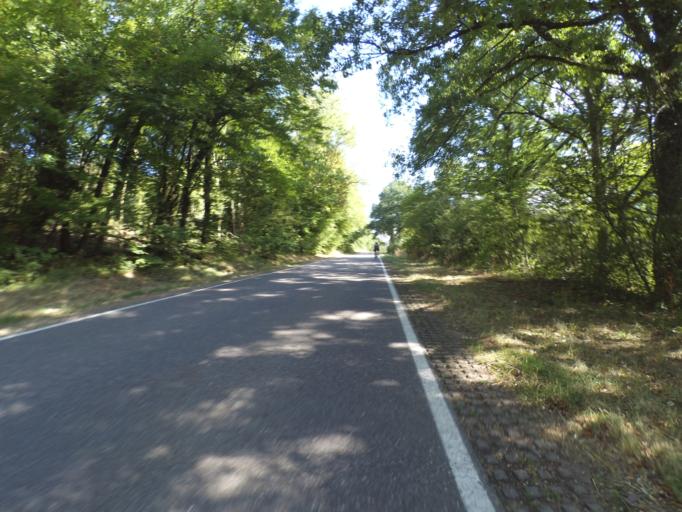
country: DE
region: Saarland
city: Perl
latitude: 49.5098
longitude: 6.4104
